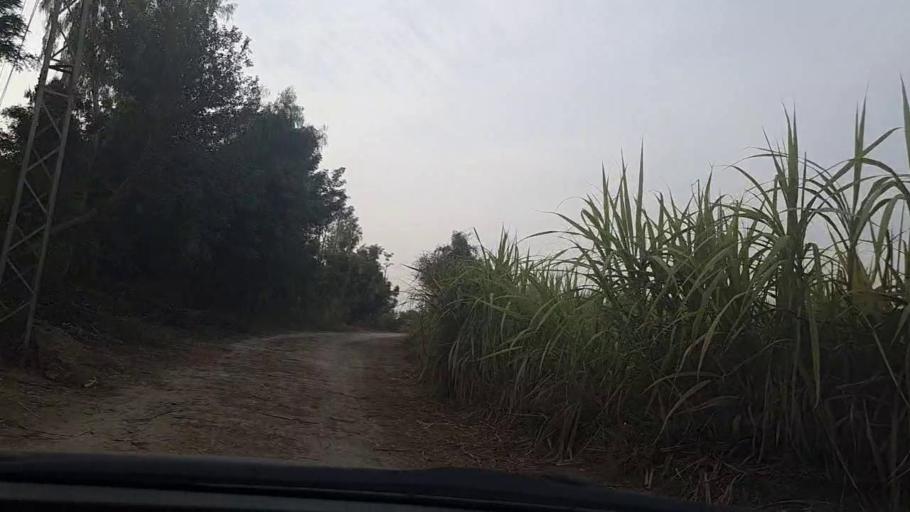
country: PK
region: Sindh
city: Daulatpur
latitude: 26.3350
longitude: 68.0392
